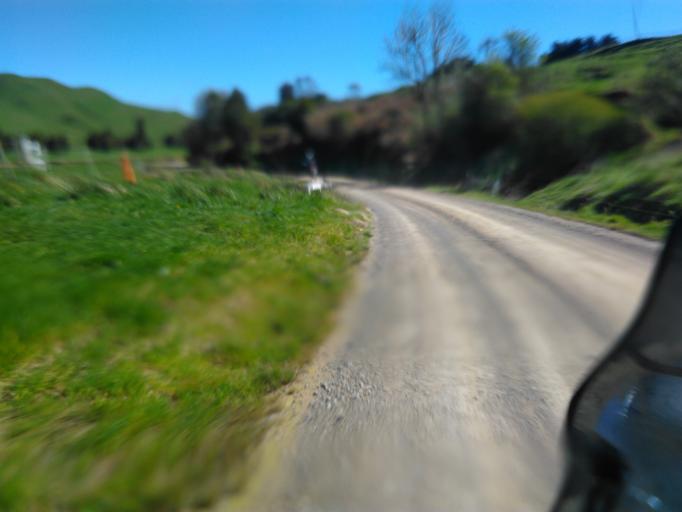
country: NZ
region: Bay of Plenty
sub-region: Opotiki District
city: Opotiki
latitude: -38.2913
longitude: 177.5469
